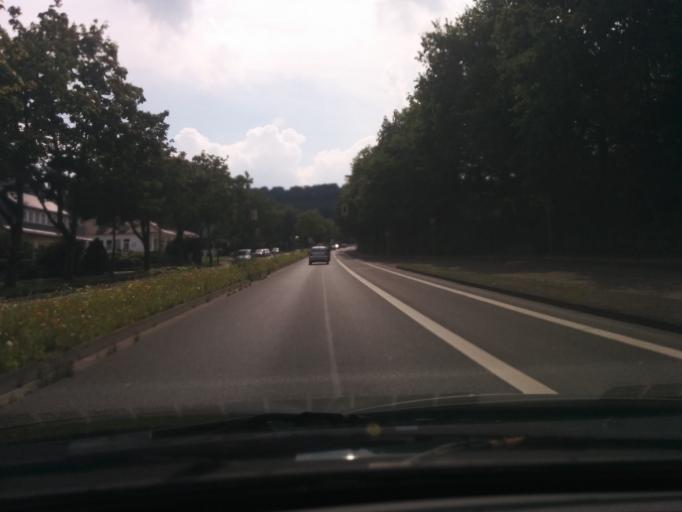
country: DE
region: North Rhine-Westphalia
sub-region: Regierungsbezirk Detmold
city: Bielefeld
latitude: 52.0355
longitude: 8.5010
